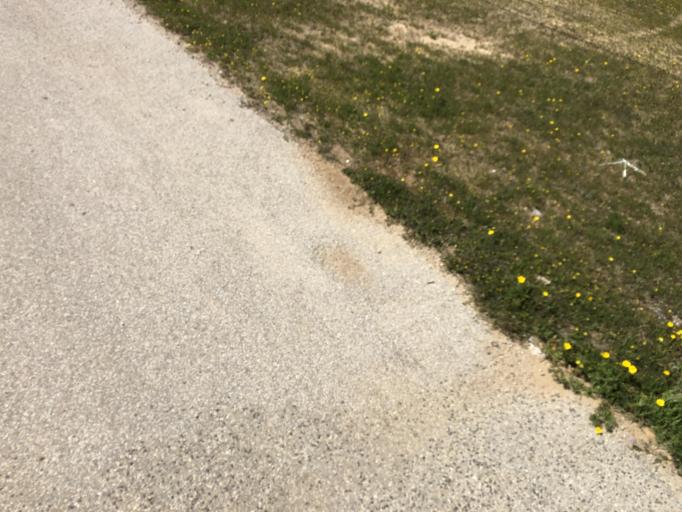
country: IL
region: Tel Aviv
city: Bat Yam
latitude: 32.0055
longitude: 34.7592
